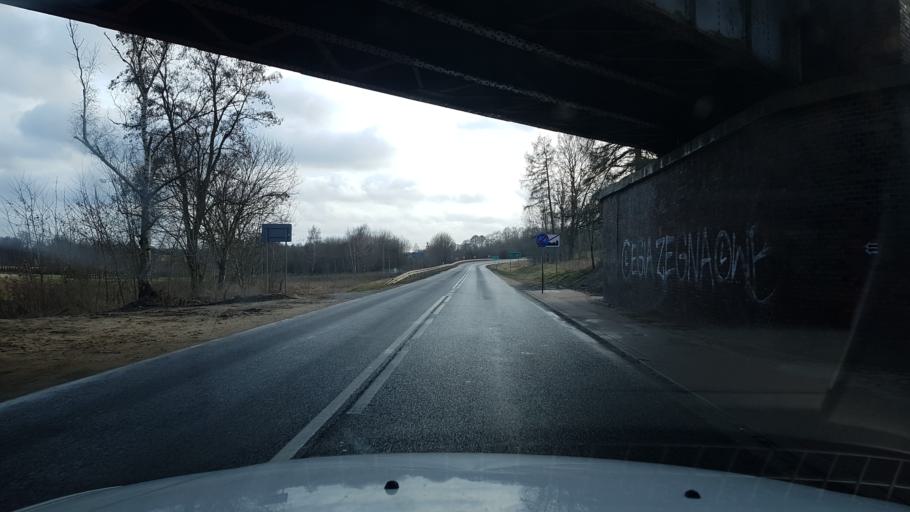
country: PL
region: West Pomeranian Voivodeship
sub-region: Powiat szczecinecki
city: Szczecinek
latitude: 53.6841
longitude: 16.6885
